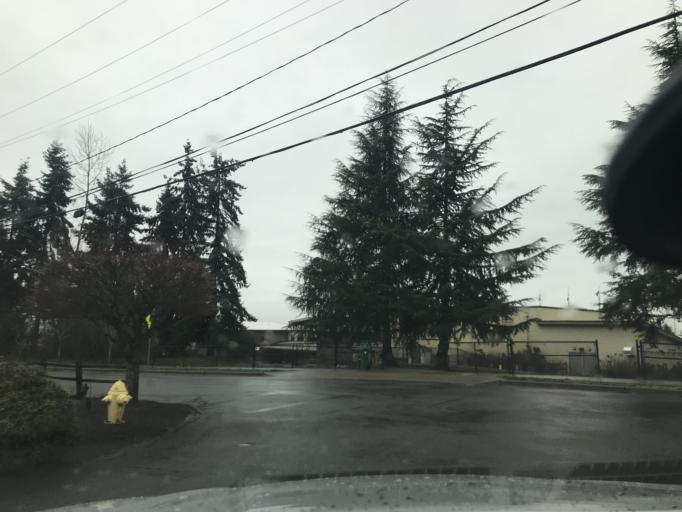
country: US
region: Washington
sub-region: King County
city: Kirkland
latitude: 47.6627
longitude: -122.1908
